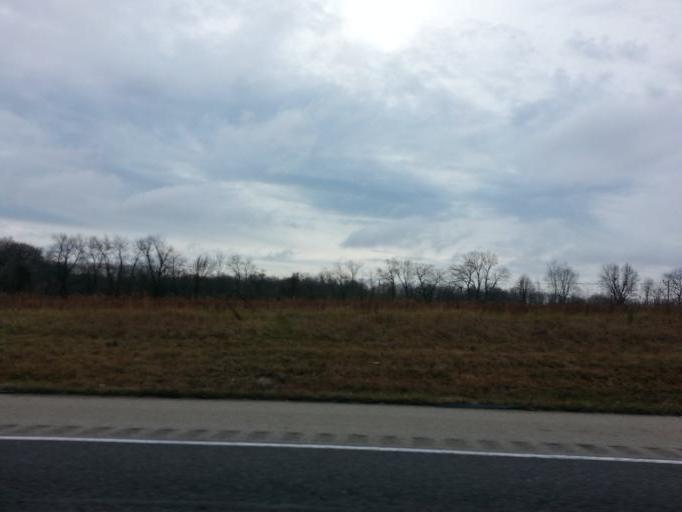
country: US
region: Indiana
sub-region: Ripley County
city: Batesville
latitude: 39.3168
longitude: -85.3021
